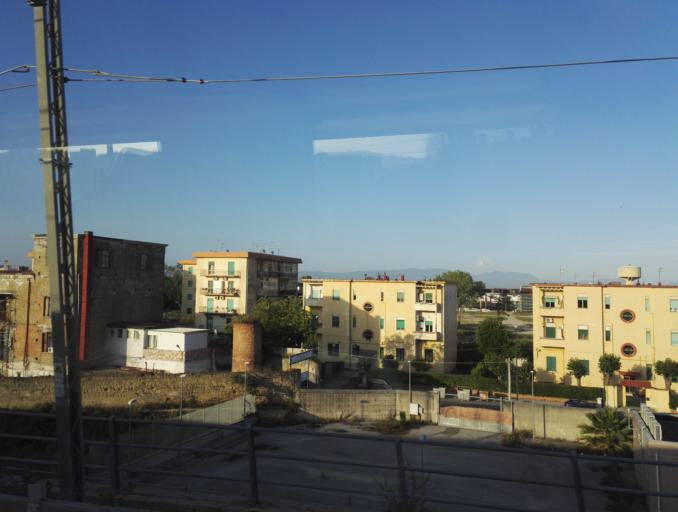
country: IT
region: Campania
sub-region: Provincia di Napoli
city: Arpino
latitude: 40.8624
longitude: 14.2965
